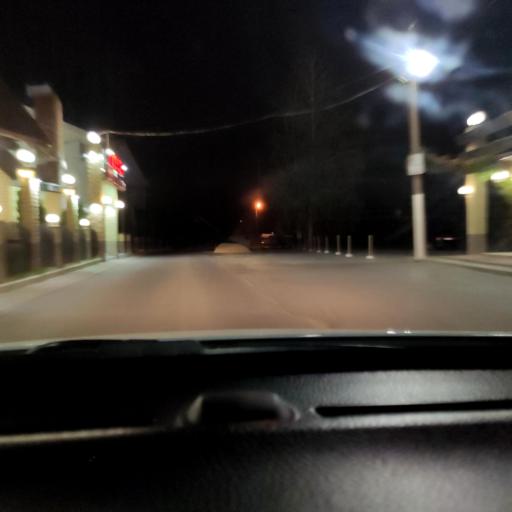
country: RU
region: Voronezj
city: Somovo
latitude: 51.6773
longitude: 39.3311
